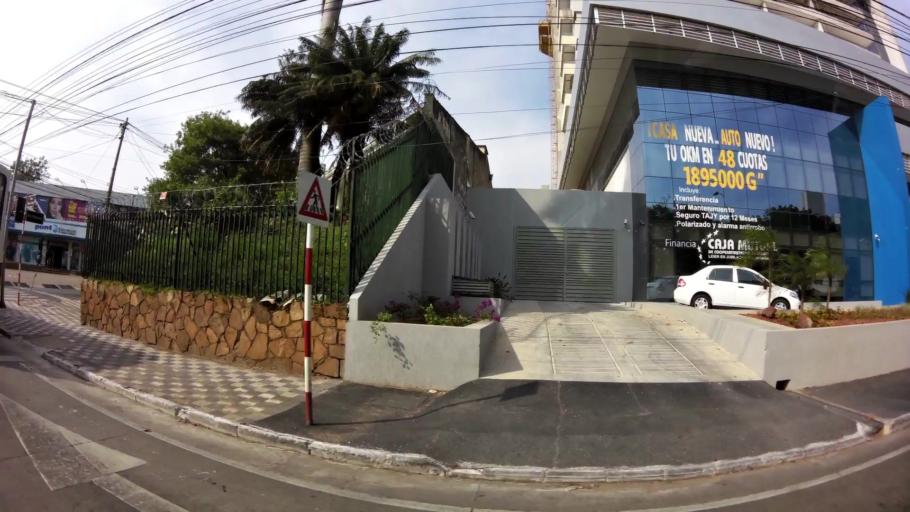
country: PY
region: Central
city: Fernando de la Mora
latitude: -25.3008
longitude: -57.5656
